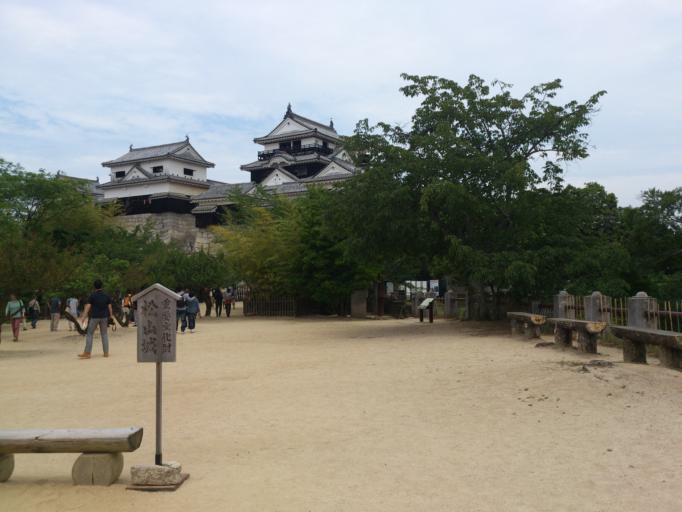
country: JP
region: Ehime
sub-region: Shikoku-chuo Shi
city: Matsuyama
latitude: 33.8448
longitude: 132.7664
